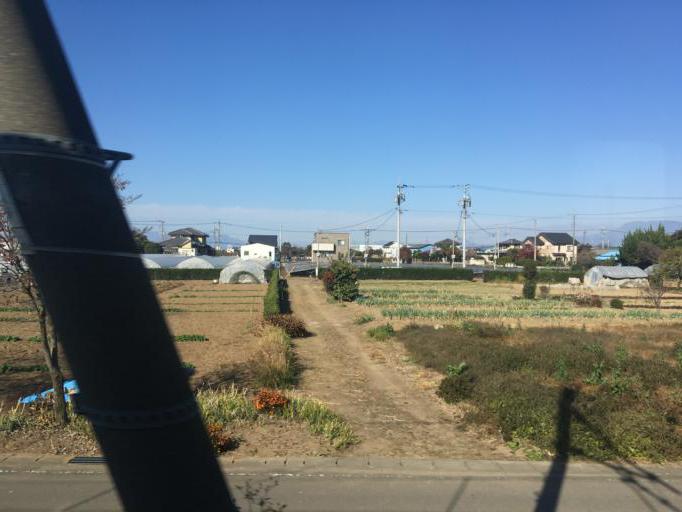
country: JP
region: Gunma
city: Isesaki
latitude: 36.3456
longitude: 139.2266
